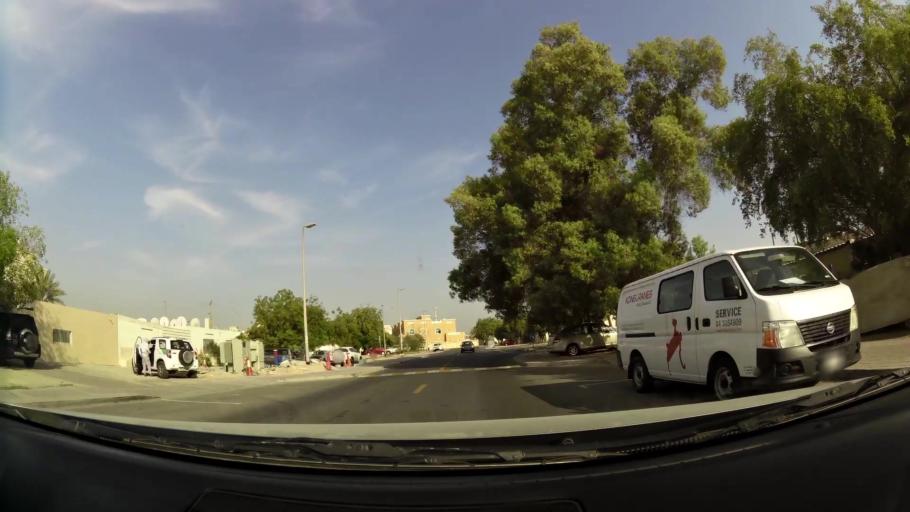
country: AE
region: Ash Shariqah
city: Sharjah
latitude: 25.2246
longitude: 55.3794
